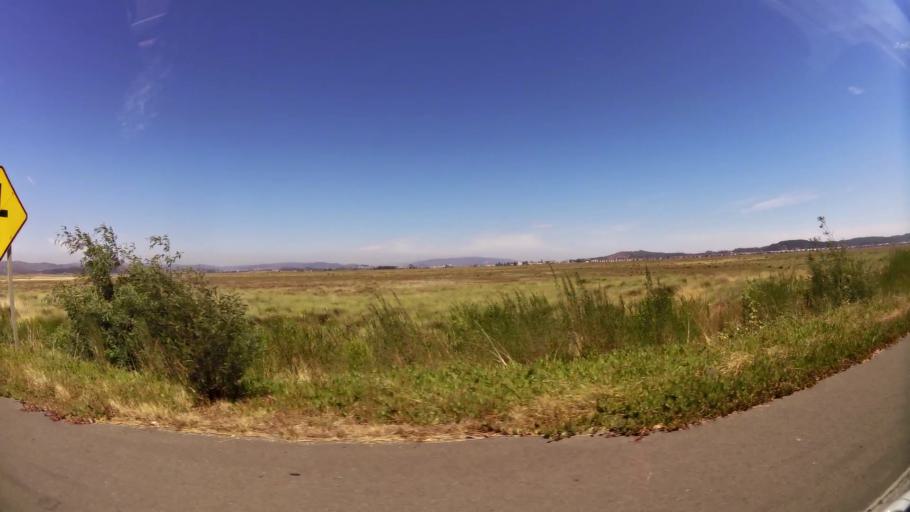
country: CL
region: Biobio
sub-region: Provincia de Concepcion
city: Talcahuano
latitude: -36.7335
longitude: -73.0720
